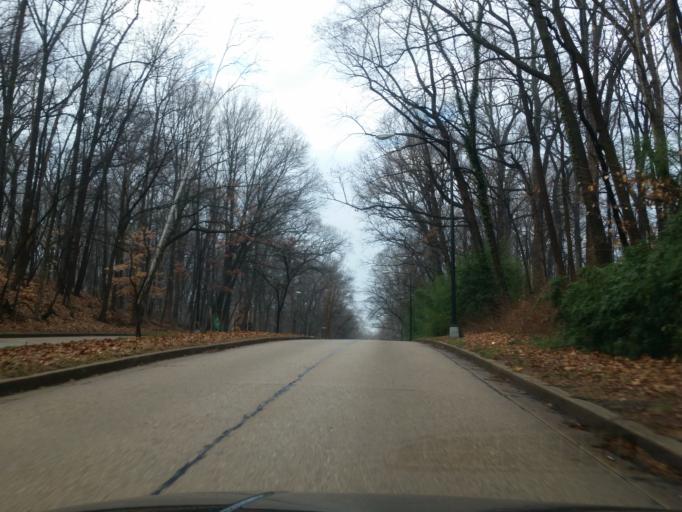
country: US
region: Maryland
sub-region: Montgomery County
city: Brookmont
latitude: 38.9405
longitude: -77.1038
